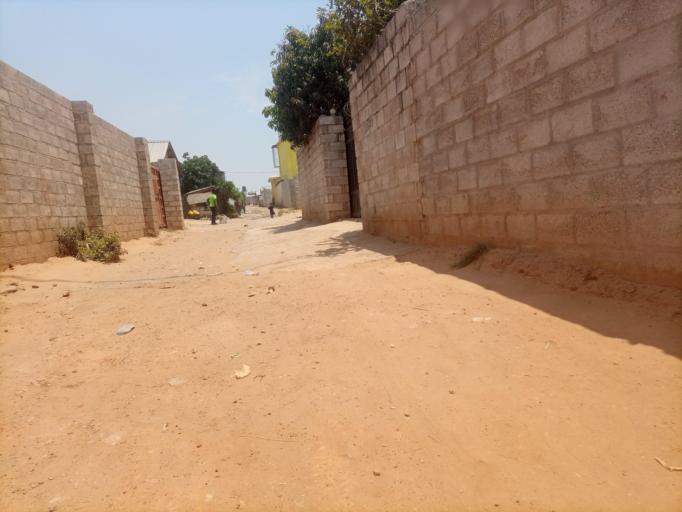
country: ZM
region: Lusaka
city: Lusaka
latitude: -15.4070
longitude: 28.3738
